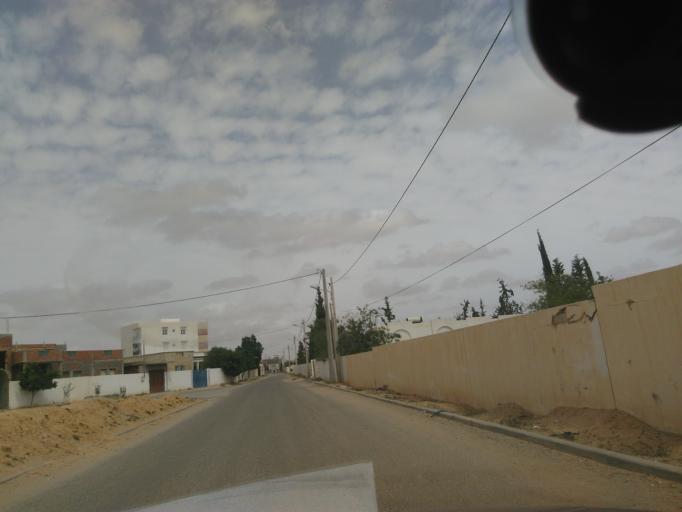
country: TN
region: Tataouine
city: Tataouine
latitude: 32.9469
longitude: 10.4730
